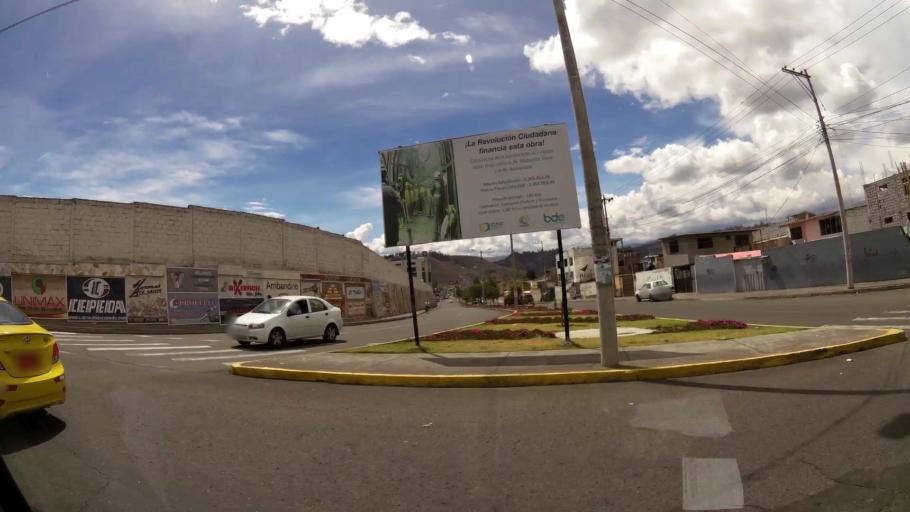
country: EC
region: Tungurahua
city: Ambato
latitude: -1.2646
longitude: -78.6229
